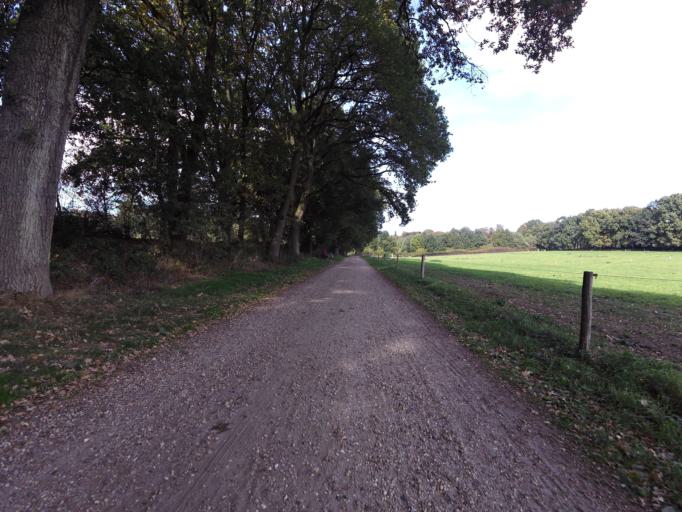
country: NL
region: Gelderland
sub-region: Gemeente Rheden
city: Rheden
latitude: 52.0125
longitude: 6.0277
